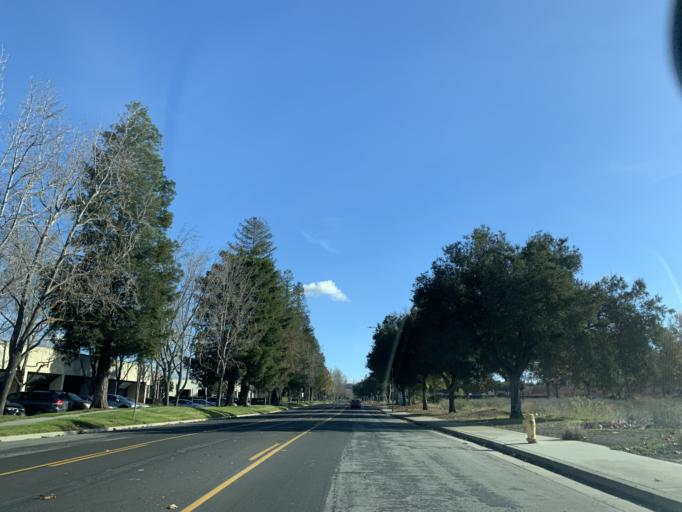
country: US
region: California
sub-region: Santa Clara County
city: Seven Trees
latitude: 37.2386
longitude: -121.7894
